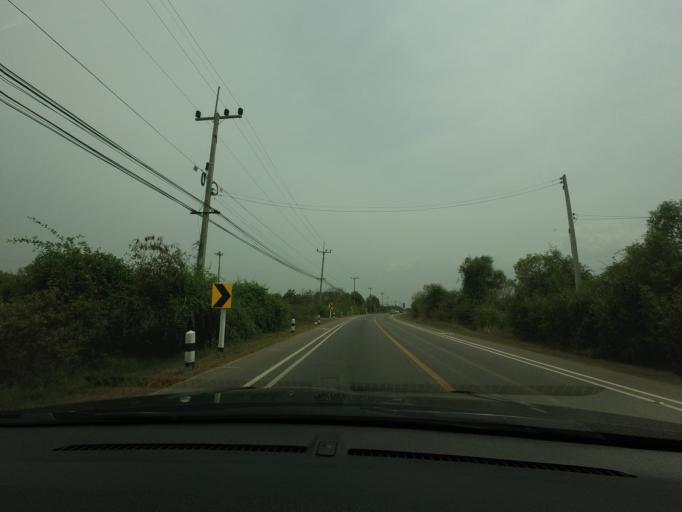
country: TH
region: Ratchaburi
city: Pak Tho
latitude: 13.3129
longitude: 99.9142
